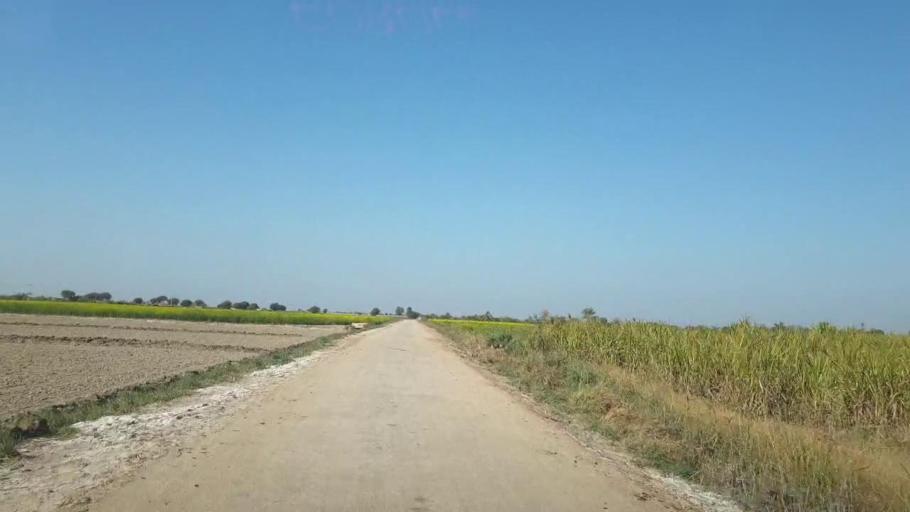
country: PK
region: Sindh
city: Mirpur Khas
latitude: 25.6363
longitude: 69.0435
